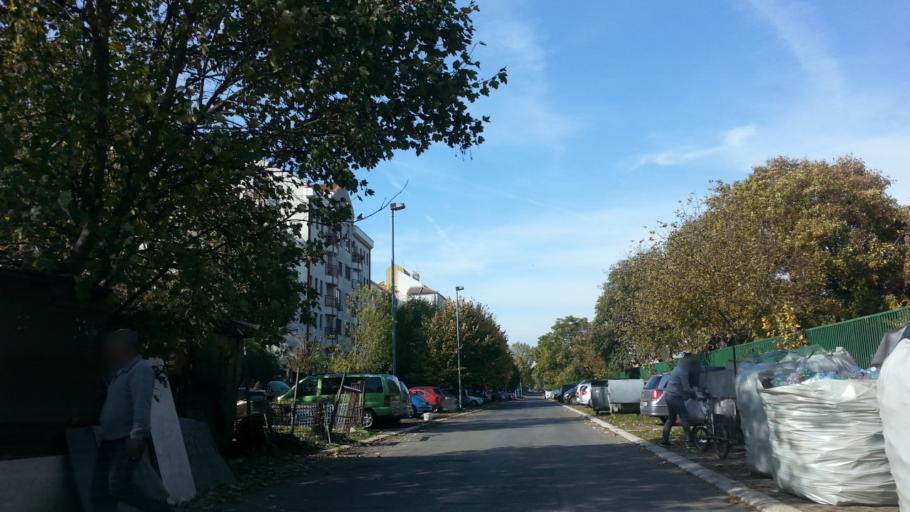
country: RS
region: Central Serbia
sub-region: Belgrade
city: Zemun
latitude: 44.8142
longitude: 20.3798
